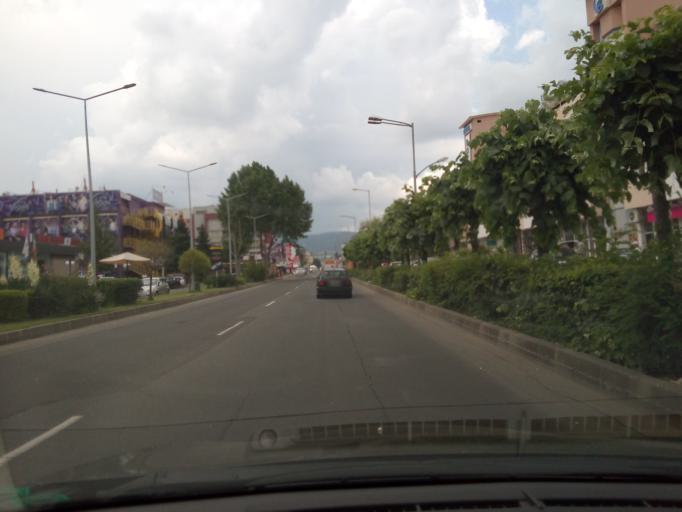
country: BG
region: Burgas
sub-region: Obshtina Nesebur
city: Nesebar
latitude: 42.6932
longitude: 27.7092
